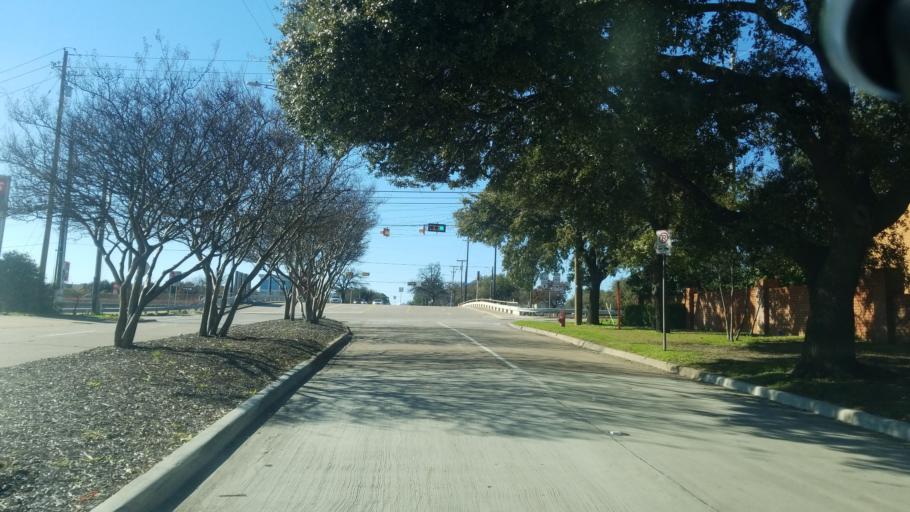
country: US
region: Texas
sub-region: Tarrant County
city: Arlington
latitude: 32.7672
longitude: -97.0620
